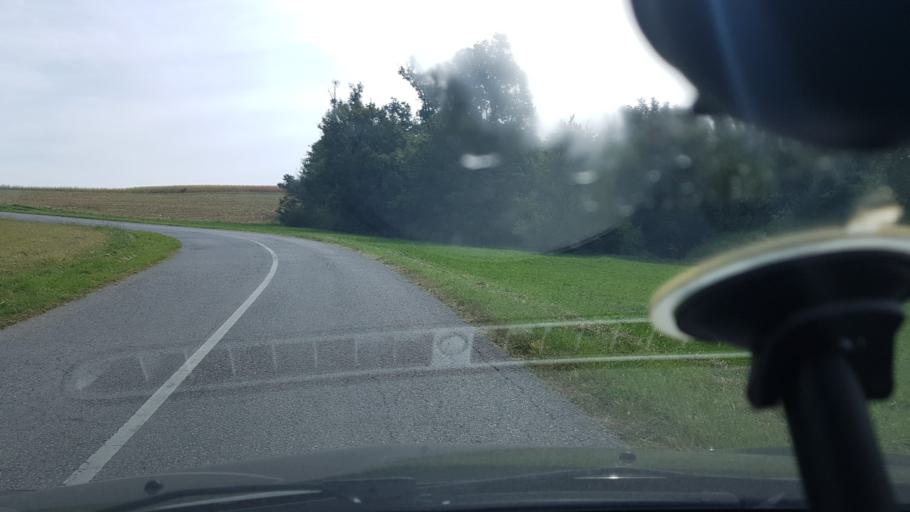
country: HR
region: Varazdinska
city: Ljubescica
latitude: 46.0984
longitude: 16.3460
